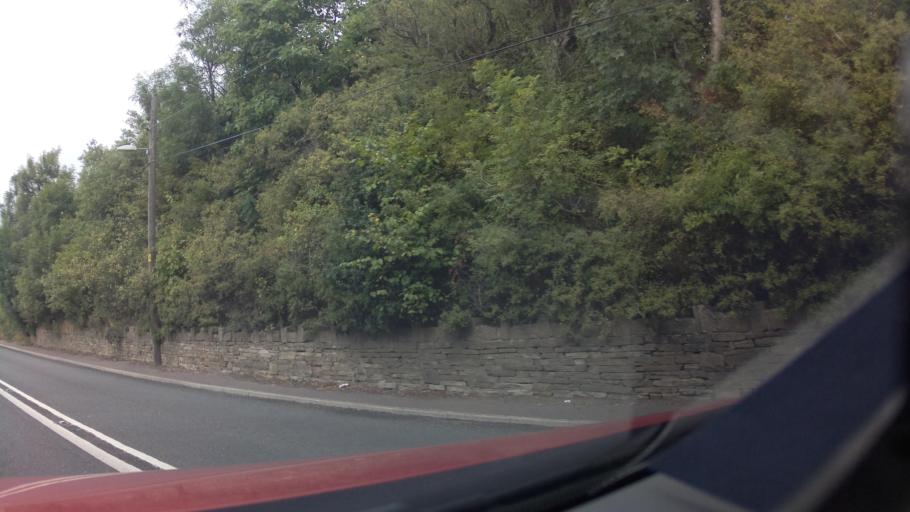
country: GB
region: England
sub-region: Kirklees
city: Kirkburton
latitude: 53.5732
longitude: -1.7312
